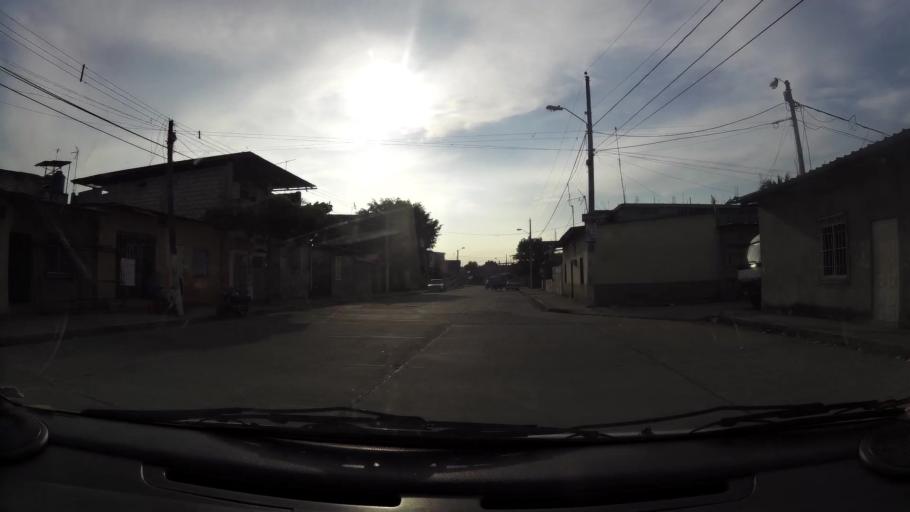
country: EC
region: Guayas
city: Eloy Alfaro
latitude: -2.0906
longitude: -79.8984
